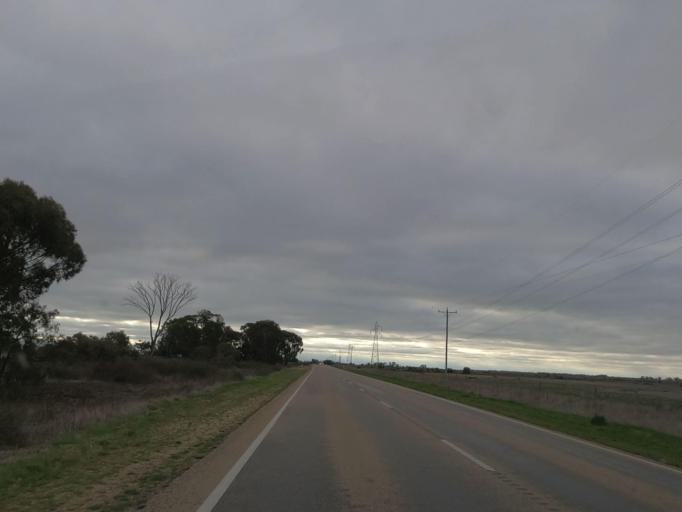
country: AU
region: Victoria
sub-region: Swan Hill
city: Swan Hill
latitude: -35.9012
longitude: 143.9462
